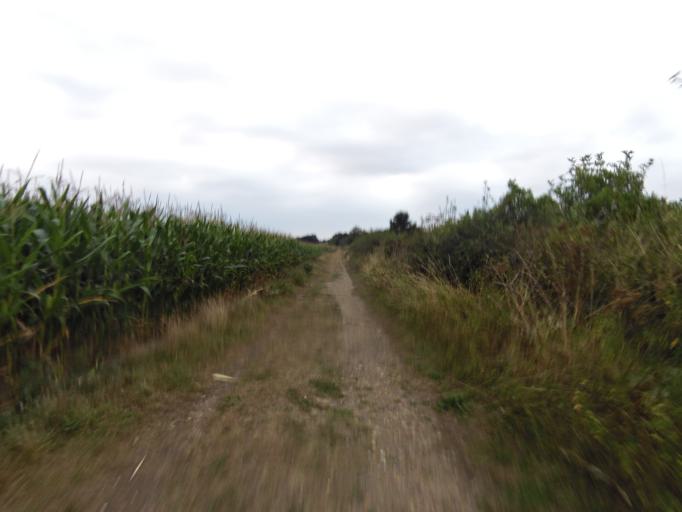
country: GB
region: England
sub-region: Hertfordshire
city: Radlett
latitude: 51.7182
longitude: -0.3159
